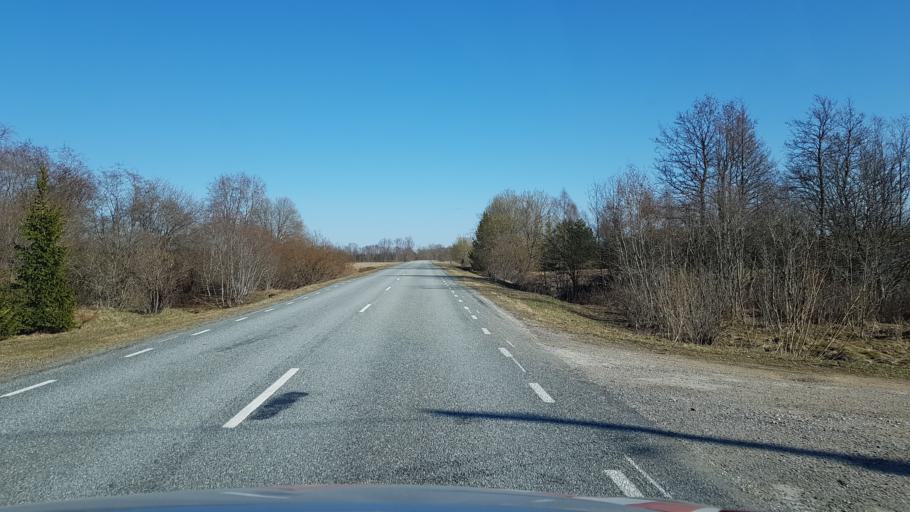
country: EE
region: Laeaene-Virumaa
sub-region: Haljala vald
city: Haljala
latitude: 59.5020
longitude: 26.1270
